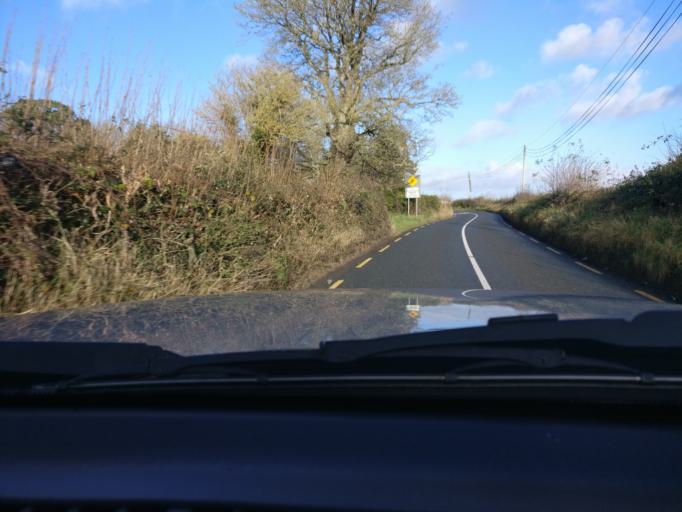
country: IE
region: Leinster
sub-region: Uibh Fhaili
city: Clara
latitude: 53.3966
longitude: -7.5818
